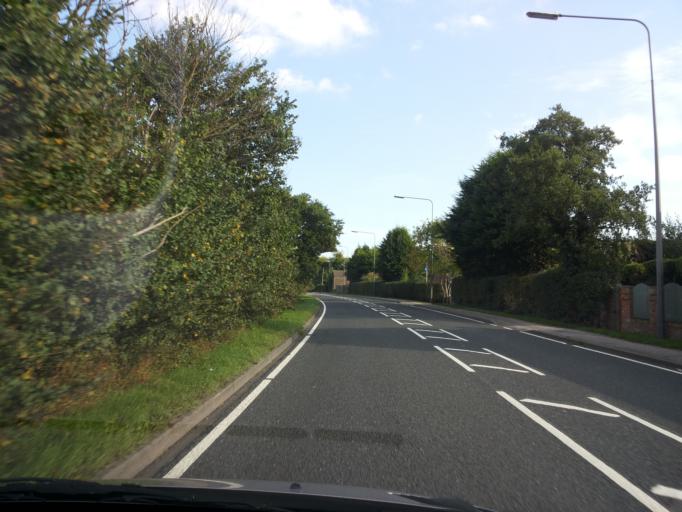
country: GB
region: England
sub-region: North Yorkshire
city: Camblesforth
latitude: 53.7282
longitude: -1.0310
